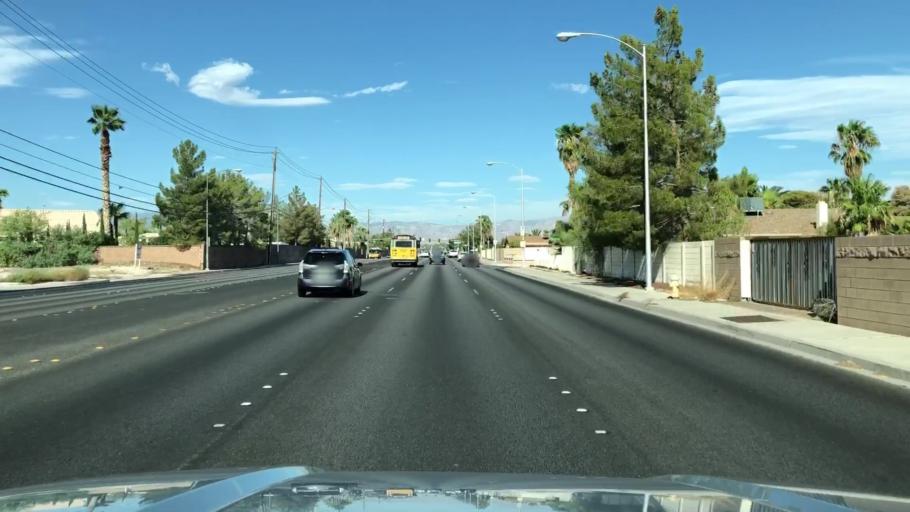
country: US
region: Nevada
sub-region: Clark County
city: Whitney
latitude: 36.0425
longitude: -115.1242
